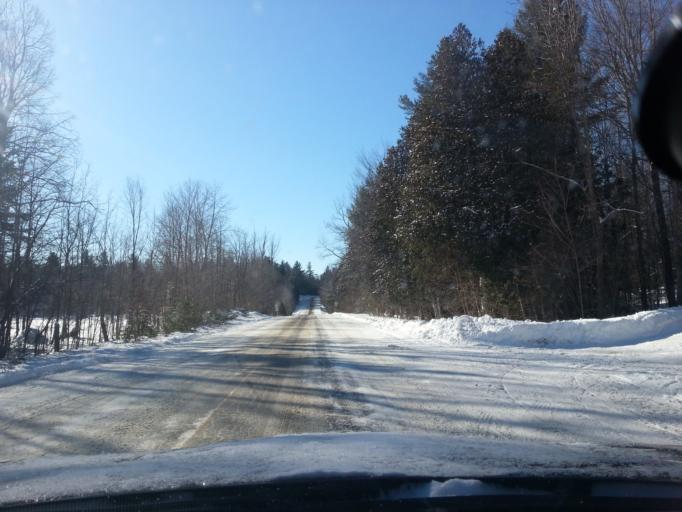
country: CA
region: Ontario
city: Arnprior
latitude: 45.2709
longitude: -76.3166
